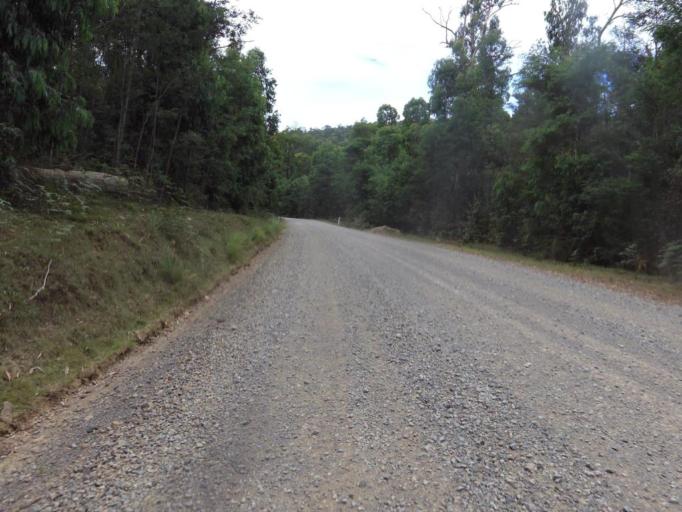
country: AU
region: Victoria
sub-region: Yarra Ranges
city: Healesville
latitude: -37.4185
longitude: 145.5644
